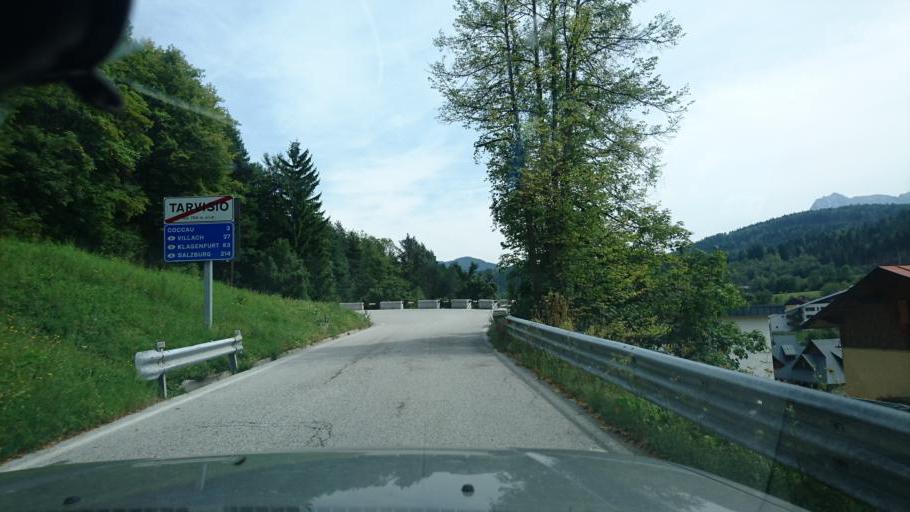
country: IT
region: Friuli Venezia Giulia
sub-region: Provincia di Udine
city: Tarvisio
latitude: 46.5051
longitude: 13.5911
